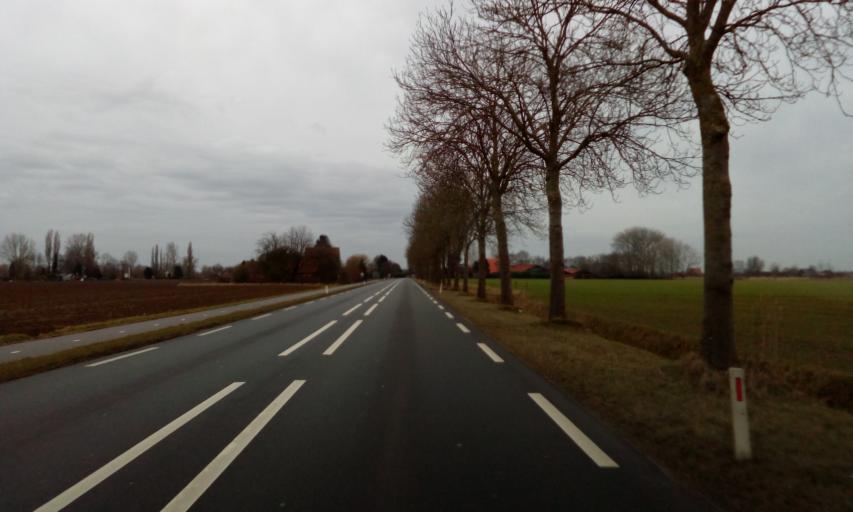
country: NL
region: North Brabant
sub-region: Gemeente Woudrichem
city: Almkerk
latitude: 51.7780
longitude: 4.9868
